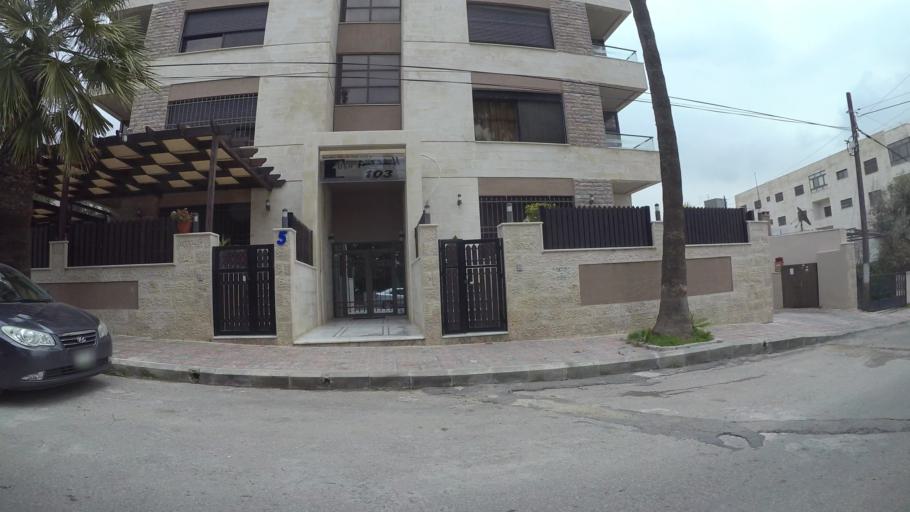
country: JO
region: Amman
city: Umm as Summaq
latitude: 31.8923
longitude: 35.8555
